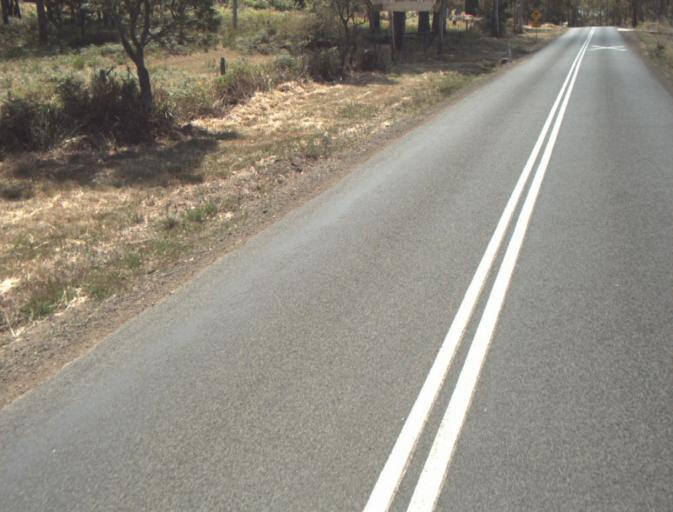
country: AU
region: Tasmania
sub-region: Launceston
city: Mayfield
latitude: -41.2809
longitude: 147.1262
